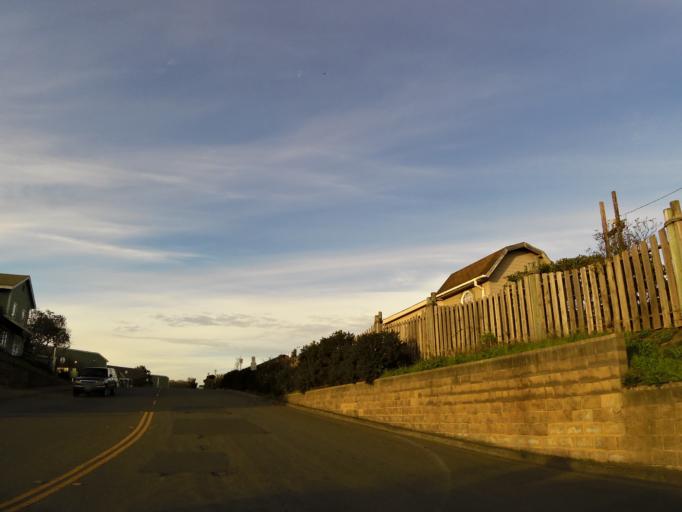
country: US
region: California
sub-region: Mendocino County
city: Fort Bragg
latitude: 39.4198
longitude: -123.8055
